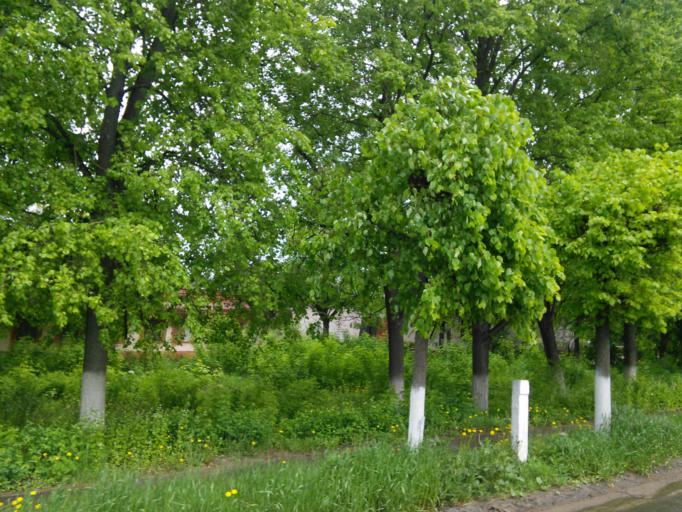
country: RU
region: Moskovskaya
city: Serpukhov
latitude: 54.9263
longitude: 37.3731
